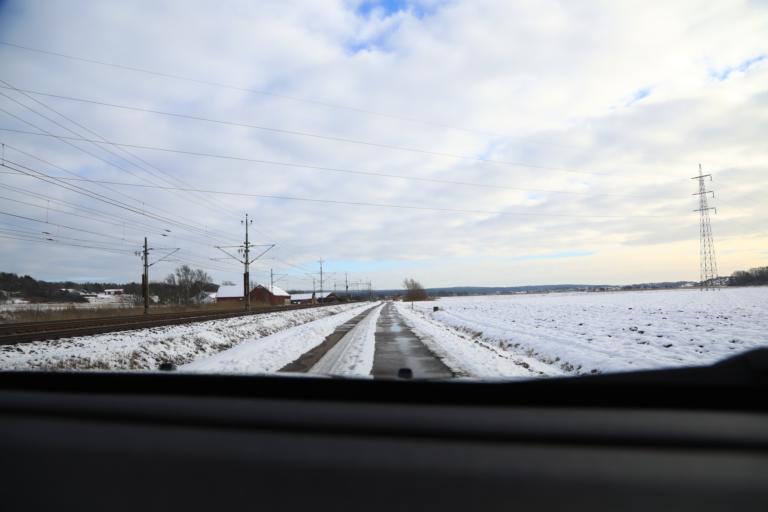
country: SE
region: Halland
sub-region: Kungsbacka Kommun
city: Frillesas
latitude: 57.2365
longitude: 12.1993
